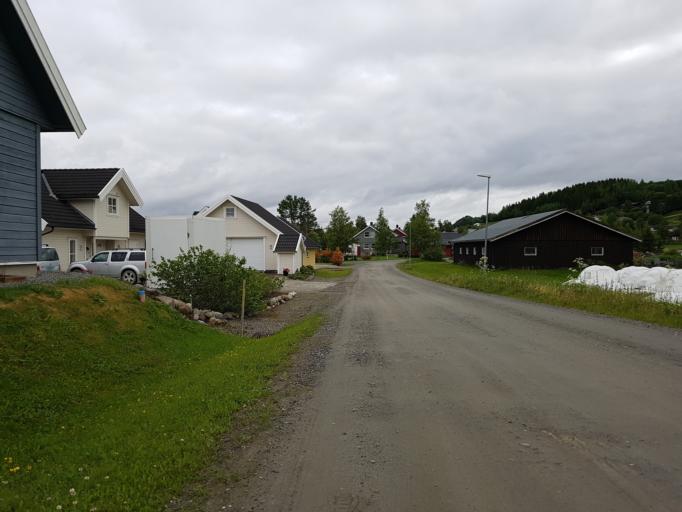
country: NO
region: Sor-Trondelag
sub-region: Selbu
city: Mebonden
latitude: 63.2227
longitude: 11.0293
